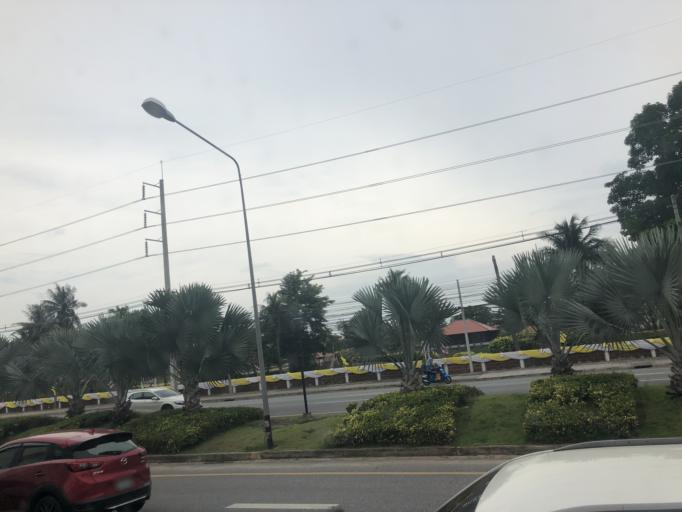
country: TH
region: Chon Buri
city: Bang Lamung
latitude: 13.0261
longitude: 100.9309
